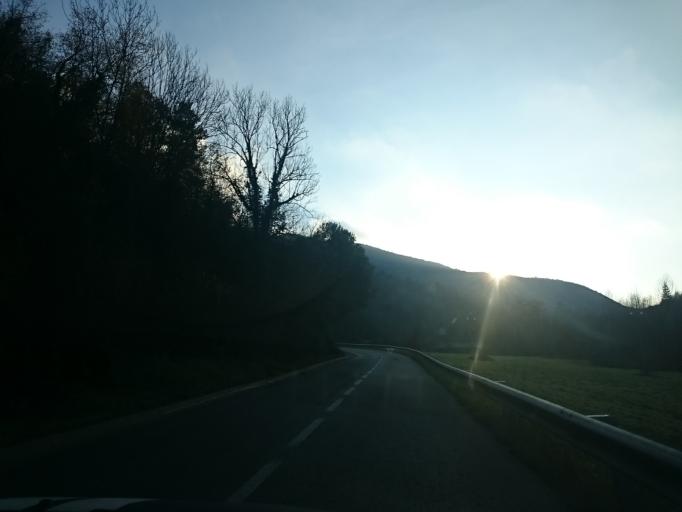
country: ES
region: Catalonia
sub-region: Provincia de Girona
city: Viladrau
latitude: 41.8564
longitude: 2.3513
